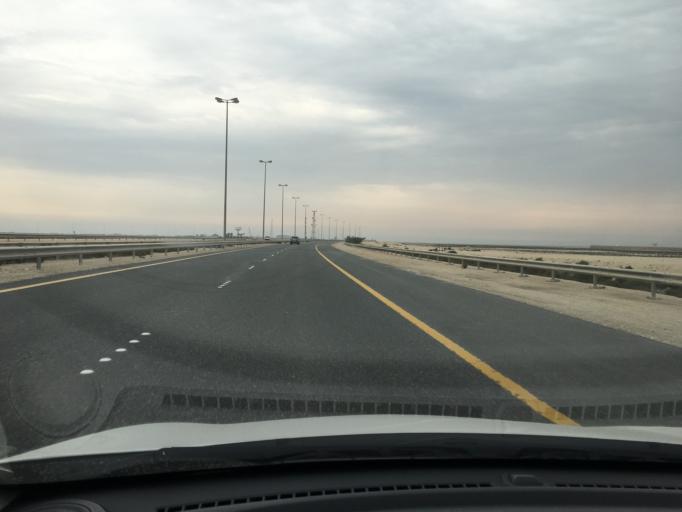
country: BH
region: Central Governorate
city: Dar Kulayb
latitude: 25.8571
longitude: 50.5850
